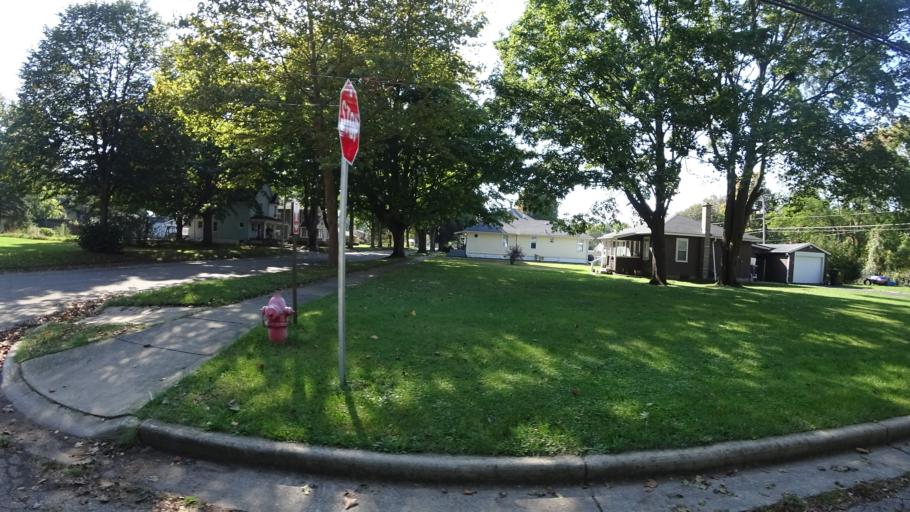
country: US
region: Michigan
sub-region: Saint Joseph County
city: Three Rivers
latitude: 41.9370
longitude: -85.6389
